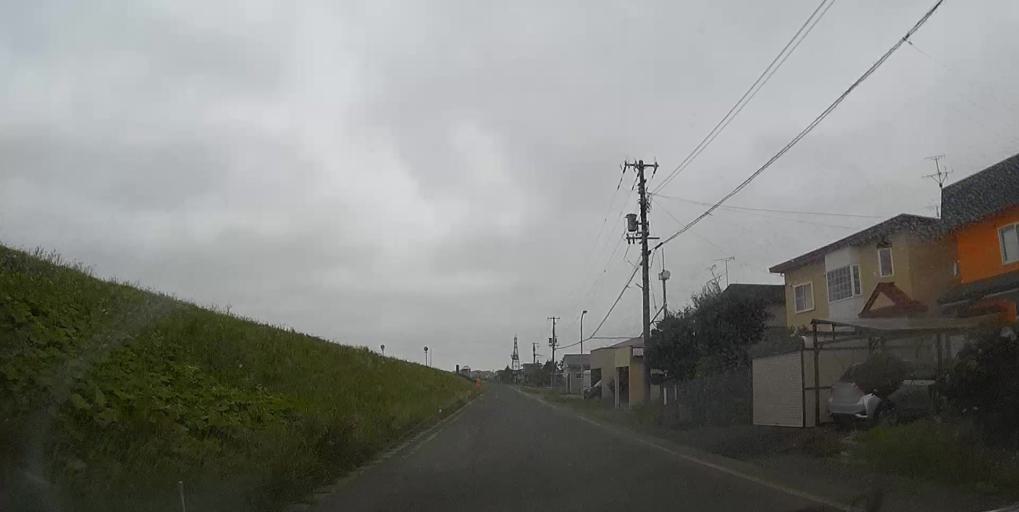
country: JP
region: Hokkaido
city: Iwanai
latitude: 42.4227
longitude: 140.0136
